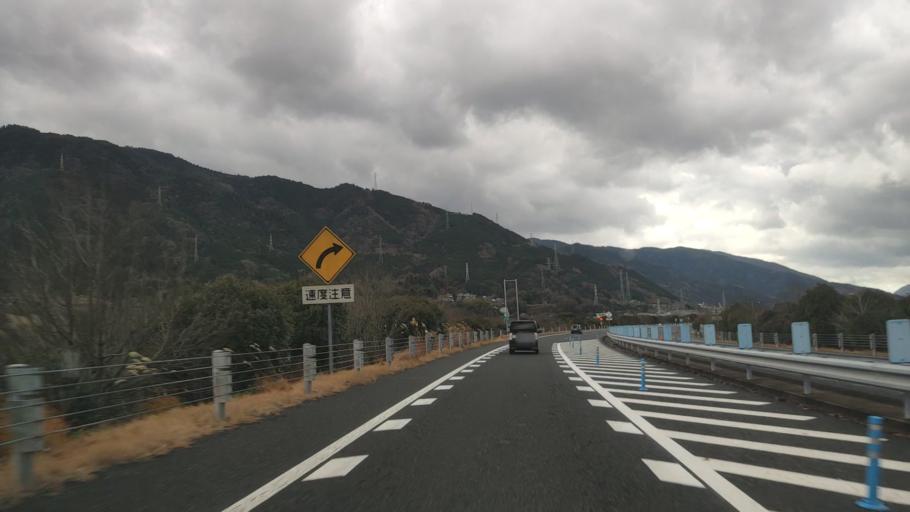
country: JP
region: Tokushima
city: Ikedacho
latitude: 34.0379
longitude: 133.9056
